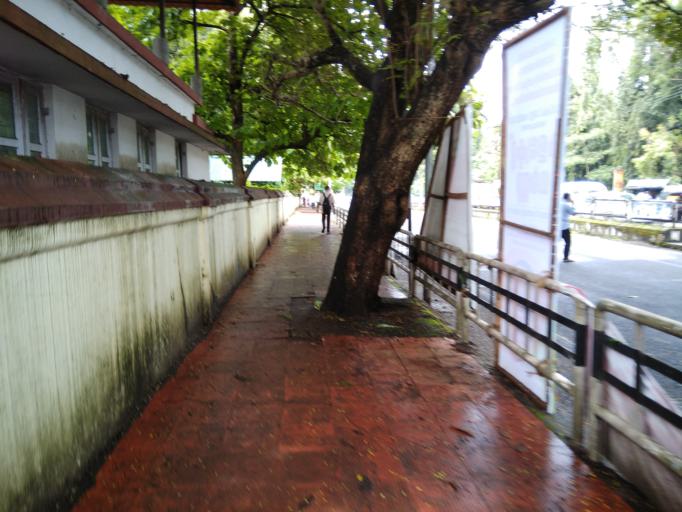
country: IN
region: Kerala
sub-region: Thrissur District
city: Trichur
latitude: 10.5310
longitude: 76.2181
